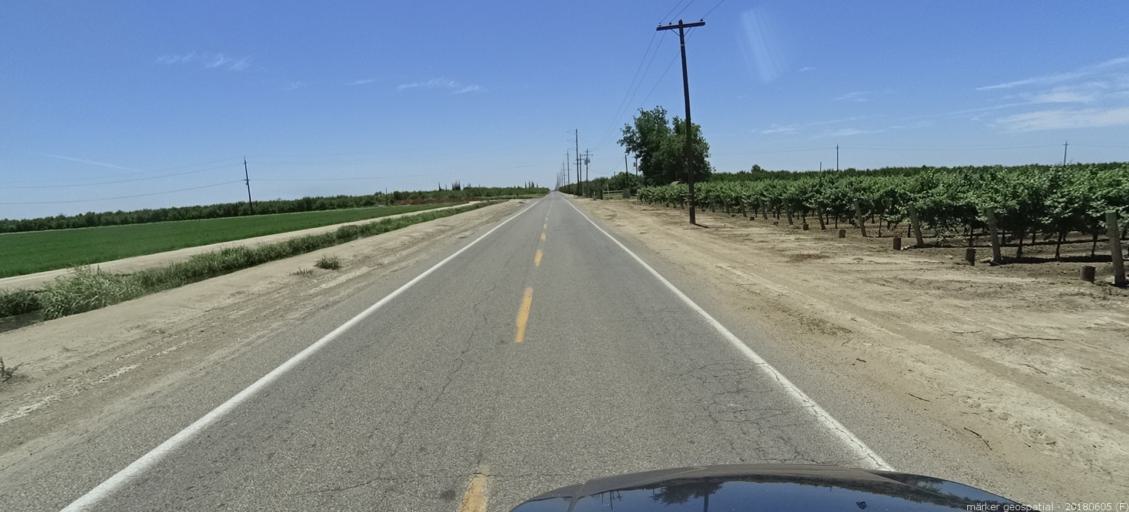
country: US
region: California
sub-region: Madera County
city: Chowchilla
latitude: 37.1286
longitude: -120.3109
